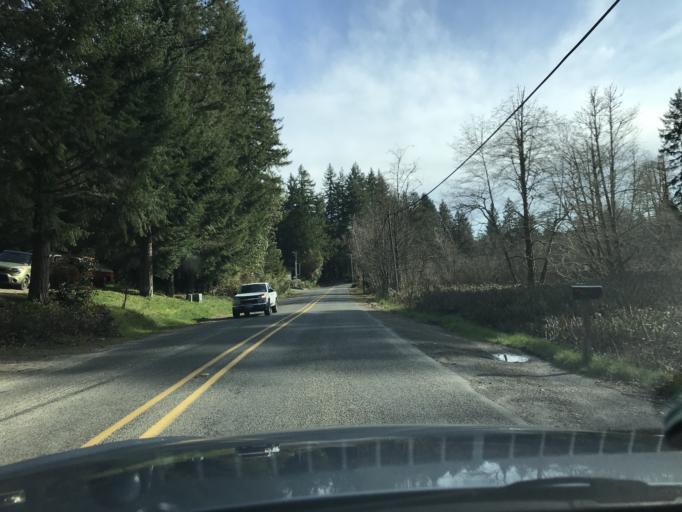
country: US
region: Washington
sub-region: Pierce County
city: Home
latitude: 47.2576
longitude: -122.7629
